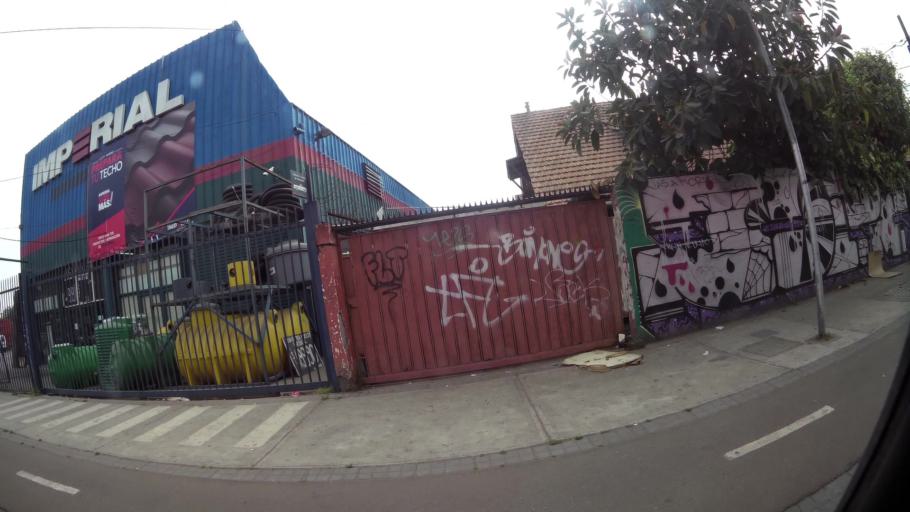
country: CL
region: Santiago Metropolitan
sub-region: Provincia de Santiago
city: Lo Prado
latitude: -33.5169
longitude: -70.7557
